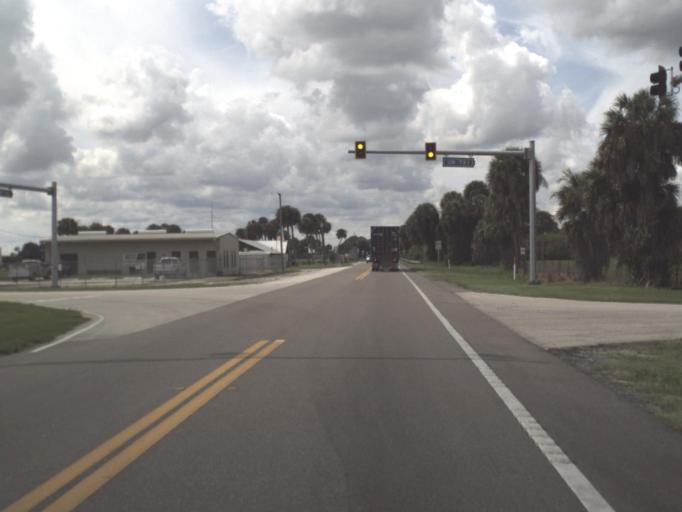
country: US
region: Florida
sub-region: Glades County
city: Buckhead Ridge
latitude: 27.2257
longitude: -81.0945
